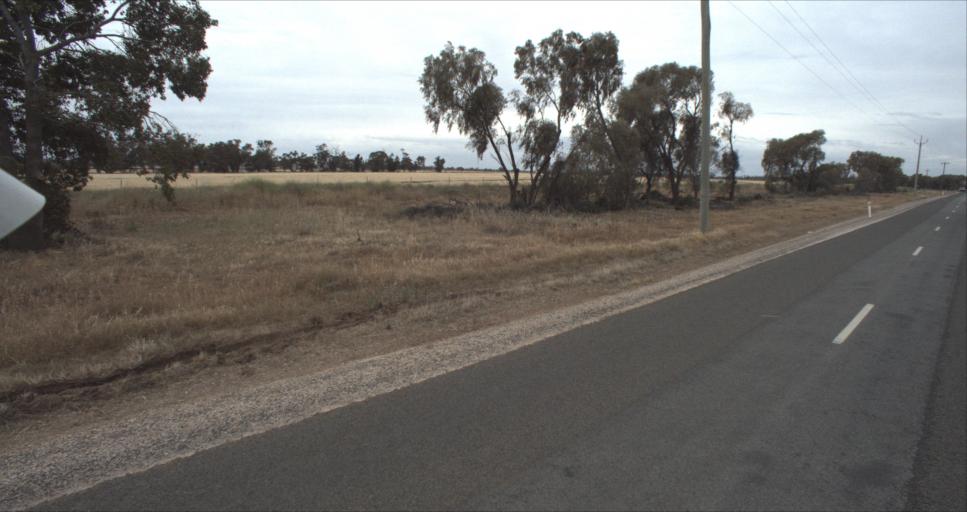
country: AU
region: New South Wales
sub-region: Leeton
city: Leeton
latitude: -34.4727
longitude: 146.3961
